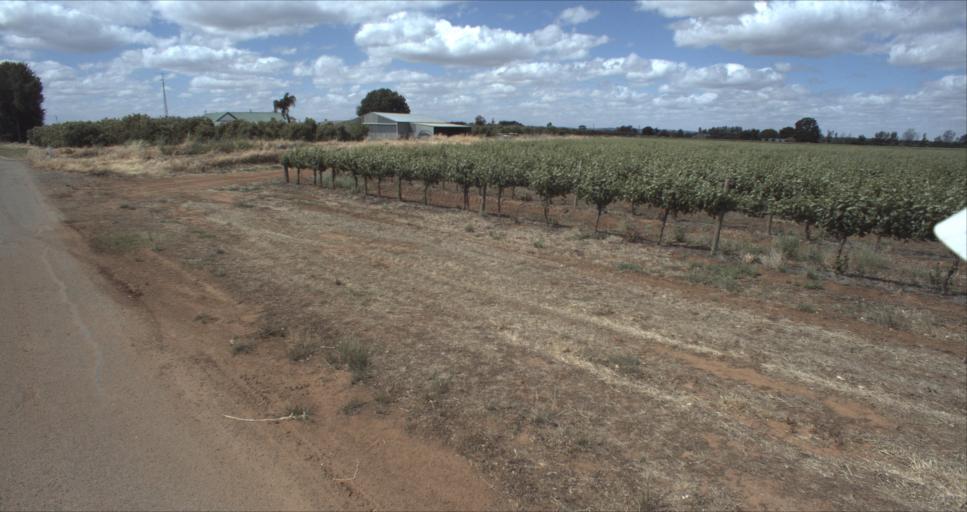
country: AU
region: New South Wales
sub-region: Leeton
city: Leeton
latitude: -34.5858
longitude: 146.3914
